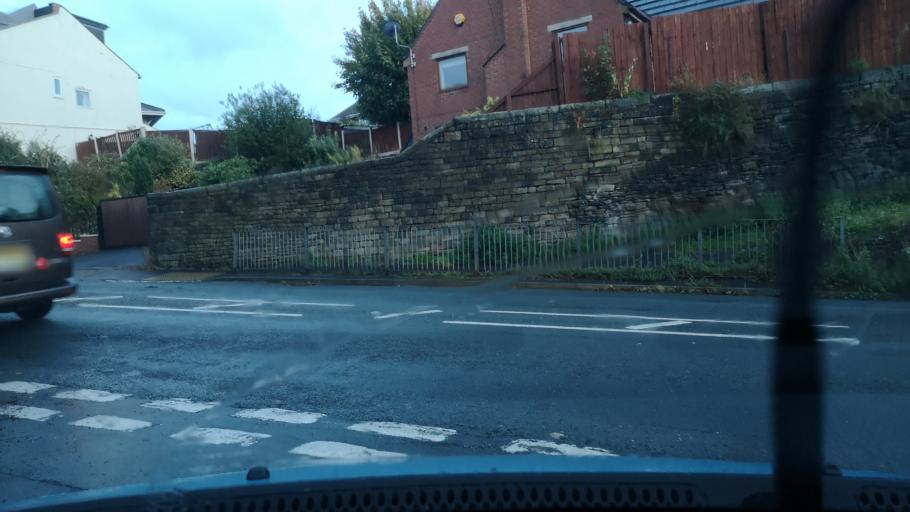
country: GB
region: England
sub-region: City and Borough of Leeds
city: Drighlington
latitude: 53.7338
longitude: -1.6515
